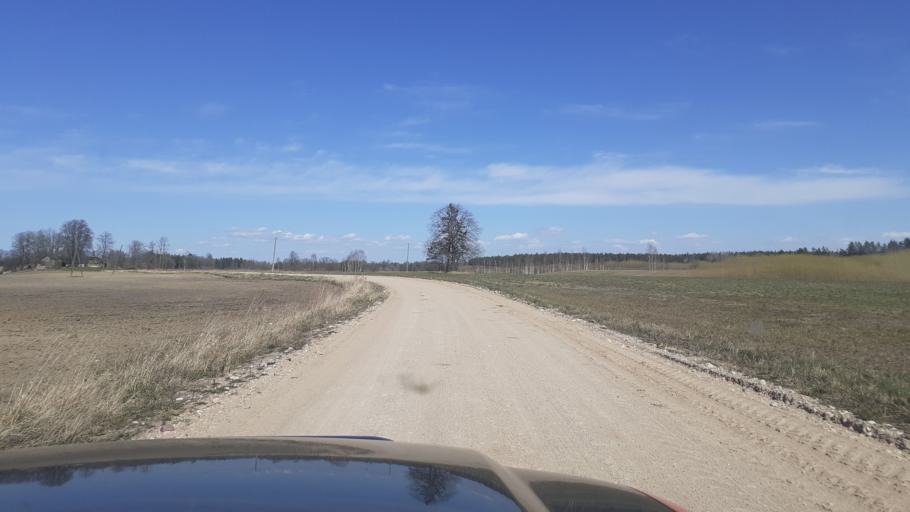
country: LV
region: Kuldigas Rajons
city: Kuldiga
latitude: 56.8505
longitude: 22.0037
